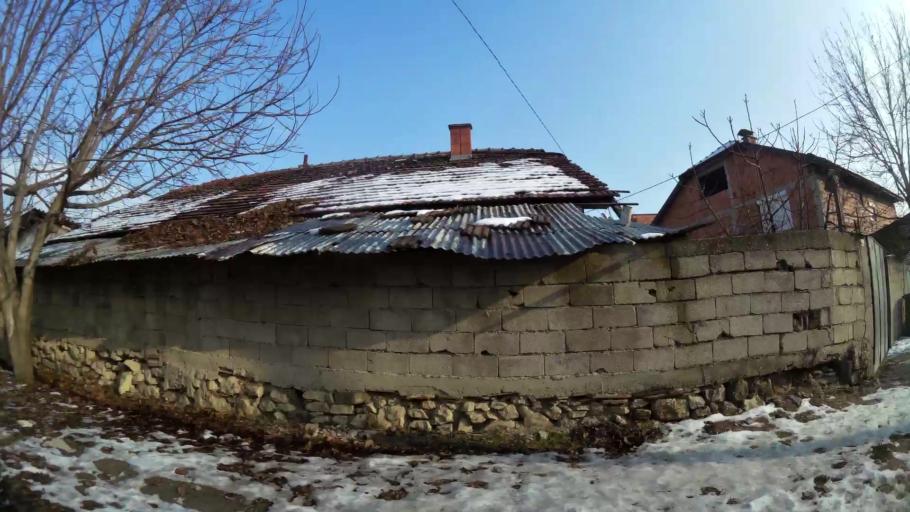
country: MK
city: Creshevo
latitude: 42.0200
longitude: 21.5090
